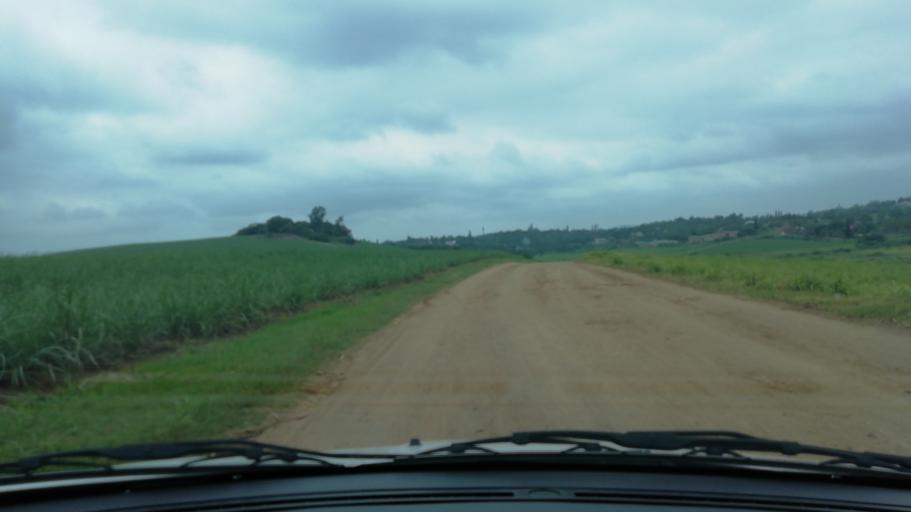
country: ZA
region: KwaZulu-Natal
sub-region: uThungulu District Municipality
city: Empangeni
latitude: -28.7328
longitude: 31.9081
